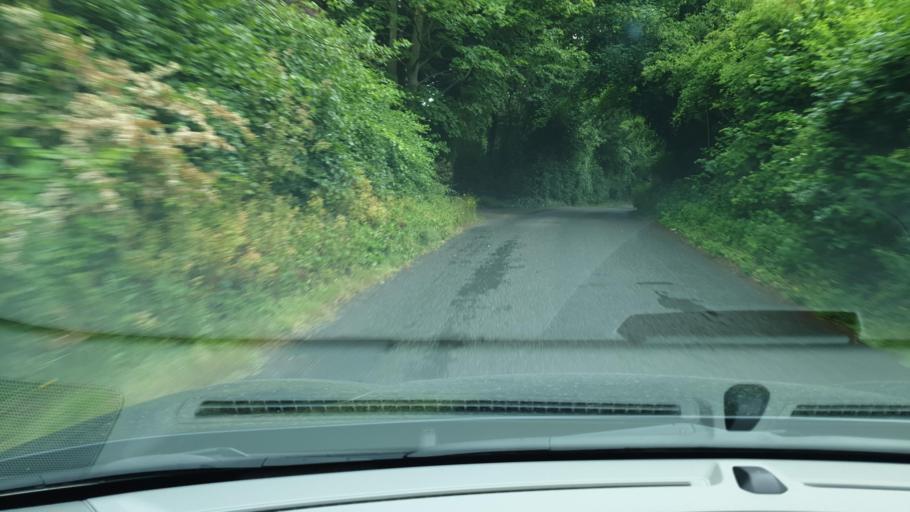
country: IE
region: Leinster
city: Hartstown
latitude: 53.4208
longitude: -6.4051
